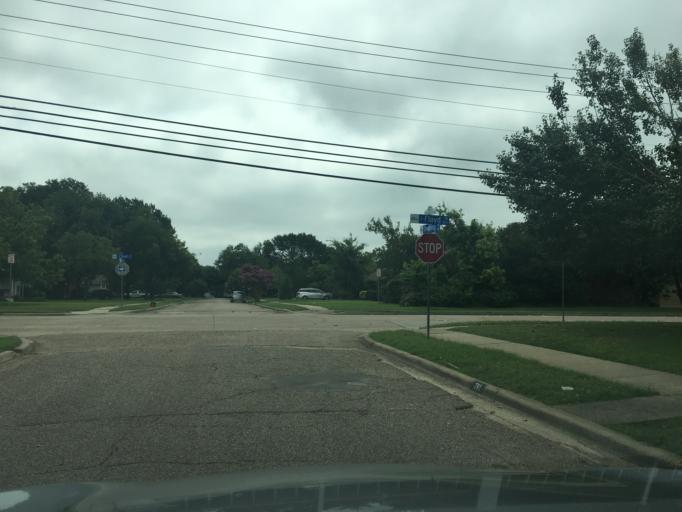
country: US
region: Texas
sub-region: Dallas County
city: Richardson
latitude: 32.9481
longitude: -96.7442
